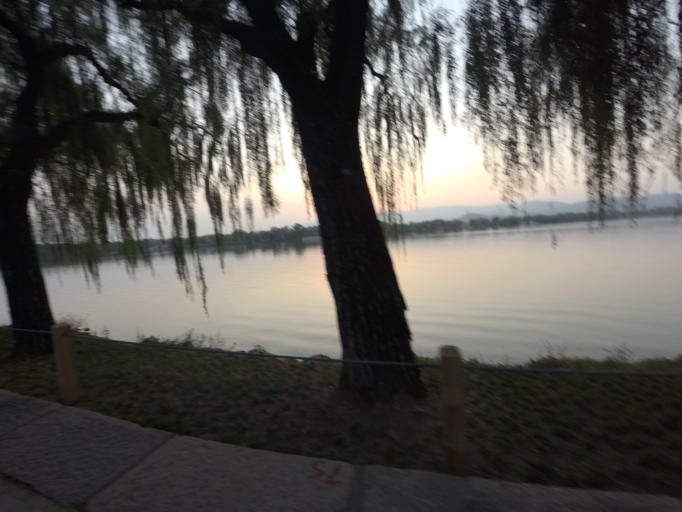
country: CN
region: Beijing
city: Haidian
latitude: 39.9853
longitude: 116.2717
